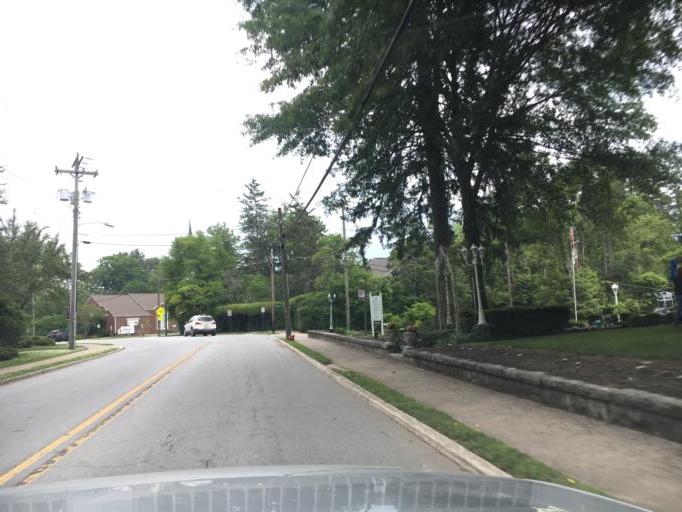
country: US
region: North Carolina
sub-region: Transylvania County
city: Brevard
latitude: 35.2312
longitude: -82.7295
